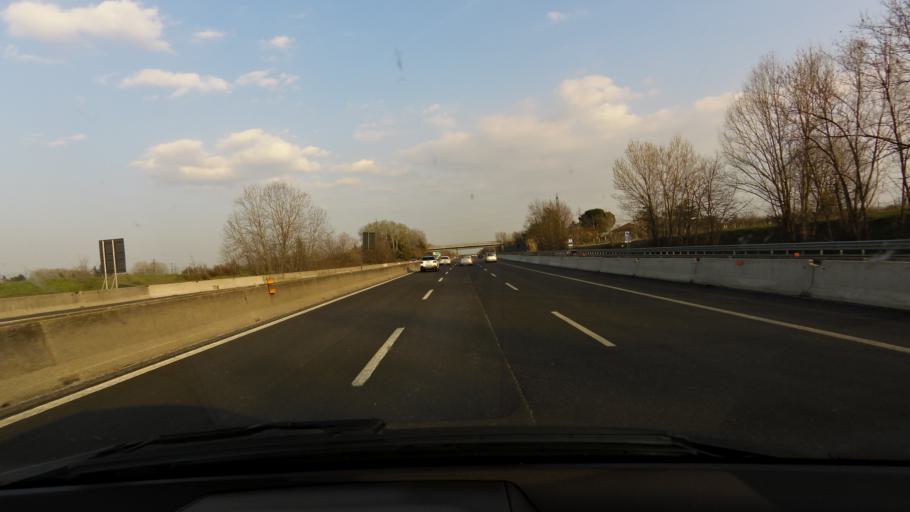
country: IT
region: Emilia-Romagna
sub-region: Provincia di Bologna
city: Villanova
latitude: 44.4799
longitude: 11.4467
